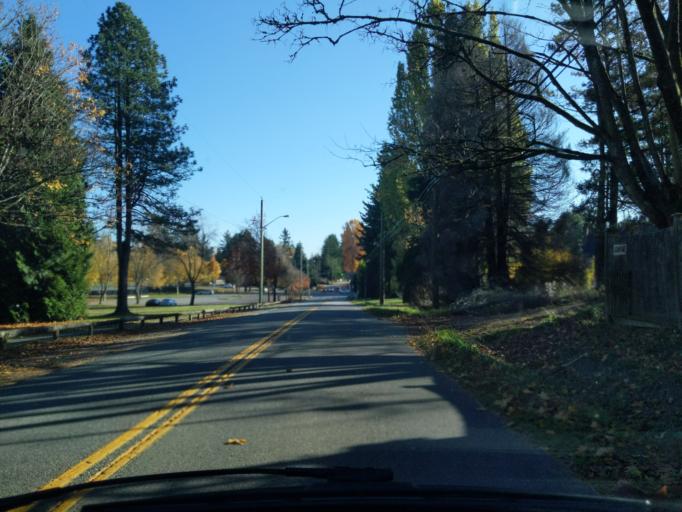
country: CA
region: British Columbia
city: New Westminster
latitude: 49.1931
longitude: -122.8650
